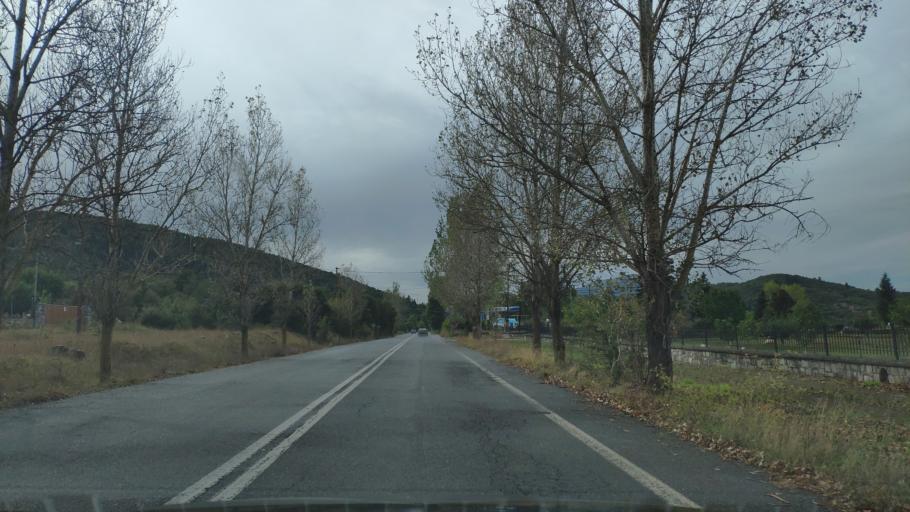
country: GR
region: Peloponnese
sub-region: Nomos Arkadias
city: Langadhia
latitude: 37.6910
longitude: 22.1958
